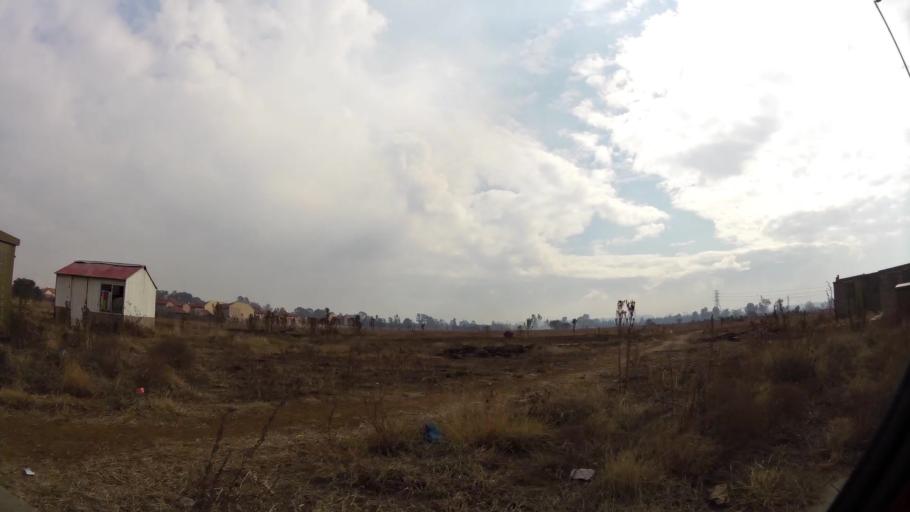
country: ZA
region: Gauteng
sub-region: Sedibeng District Municipality
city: Vanderbijlpark
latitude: -26.6800
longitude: 27.8428
